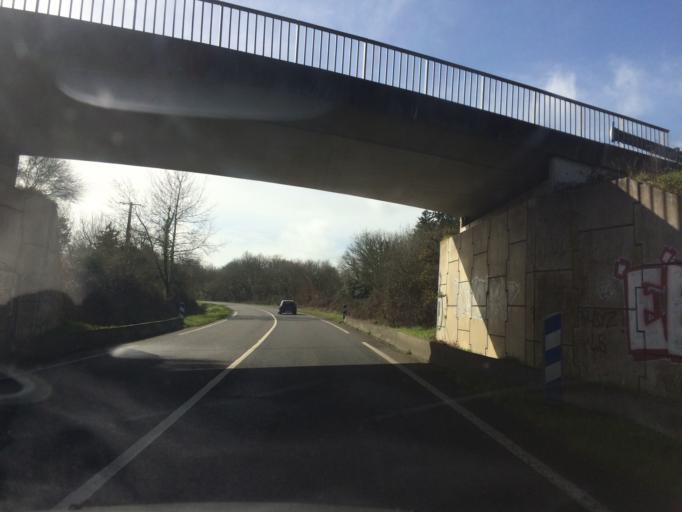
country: FR
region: Pays de la Loire
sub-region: Departement de la Loire-Atlantique
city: Besne
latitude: 47.4075
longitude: -2.0938
